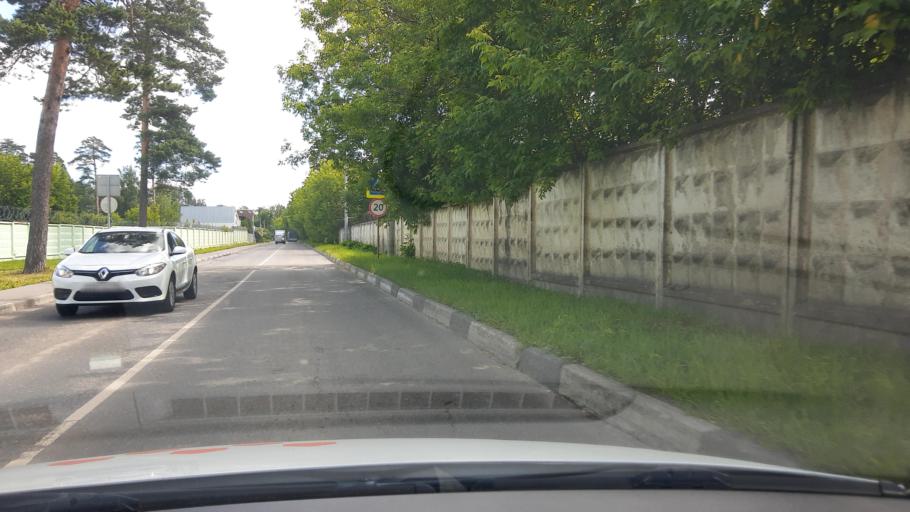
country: RU
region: Moskovskaya
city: Noginsk
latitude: 55.8771
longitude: 38.4475
